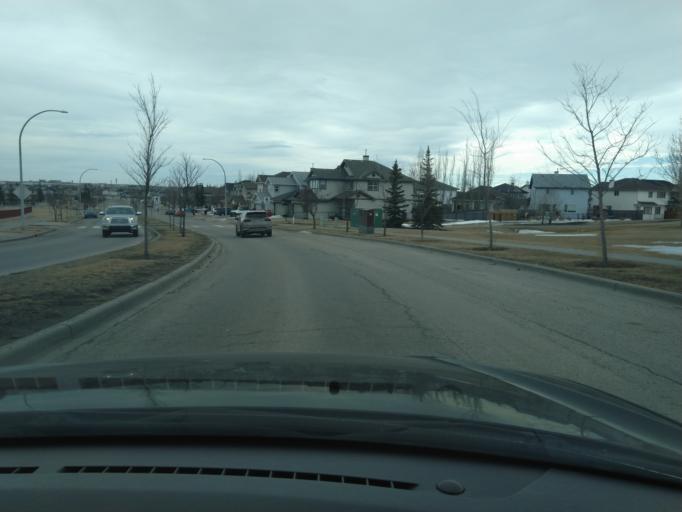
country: CA
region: Alberta
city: Calgary
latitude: 51.1677
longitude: -114.0627
